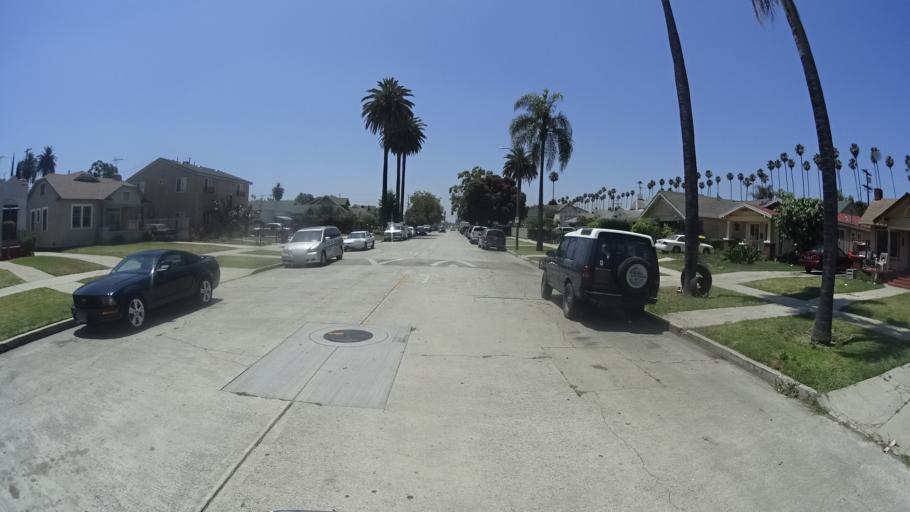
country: US
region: California
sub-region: Los Angeles County
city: View Park-Windsor Hills
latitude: 34.0020
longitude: -118.3193
